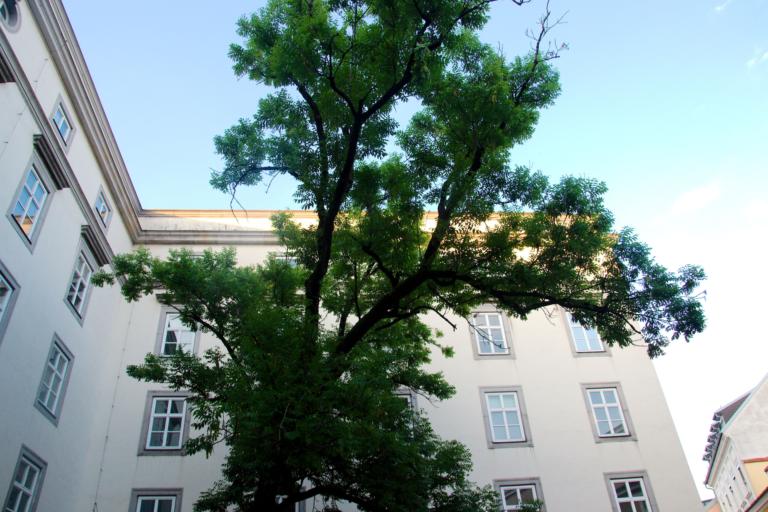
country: AT
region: Upper Austria
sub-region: Linz Stadt
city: Linz
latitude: 48.3068
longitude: 14.2867
